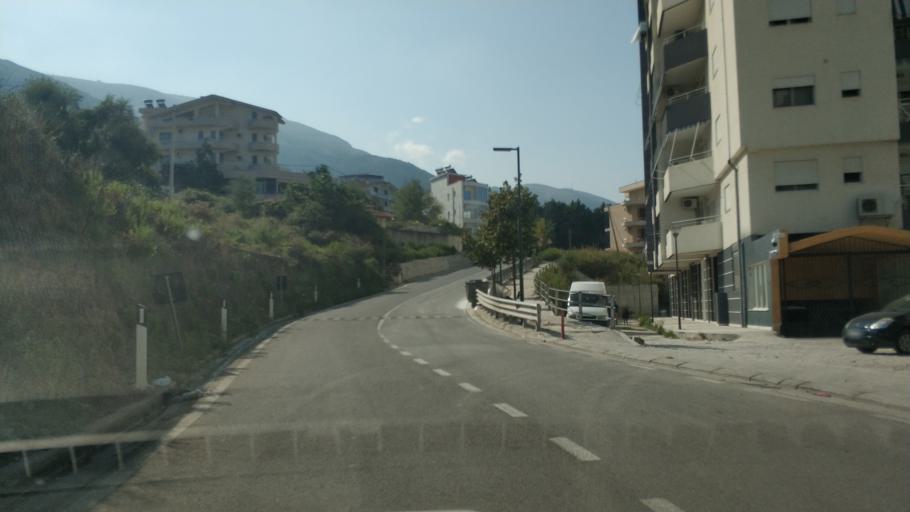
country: AL
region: Vlore
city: Vlore
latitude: 40.4361
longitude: 19.4966
